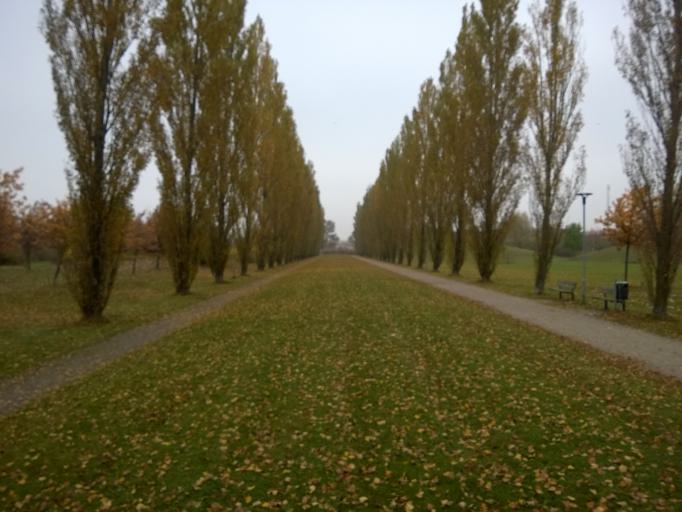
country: SE
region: Skane
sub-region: Burlovs Kommun
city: Arloev
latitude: 55.6000
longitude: 13.0526
